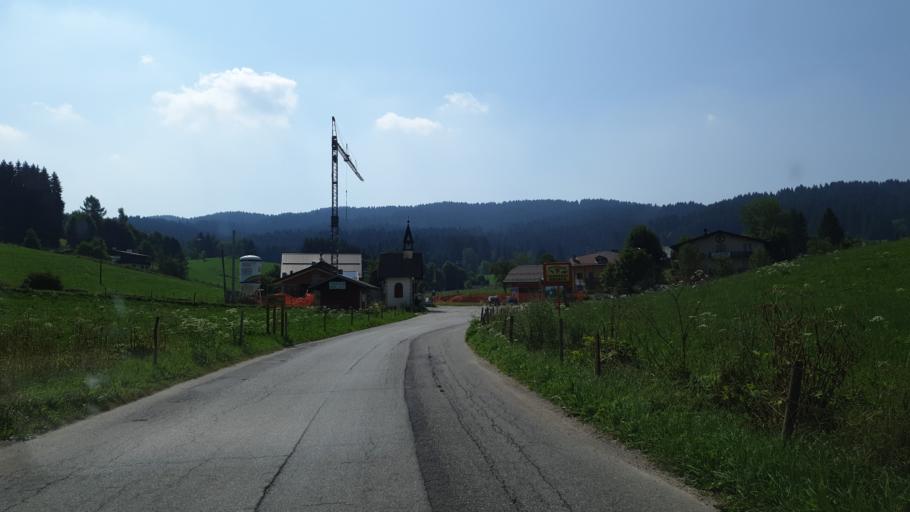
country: IT
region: Veneto
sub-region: Provincia di Vicenza
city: Asiago
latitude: 45.8581
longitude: 11.5000
